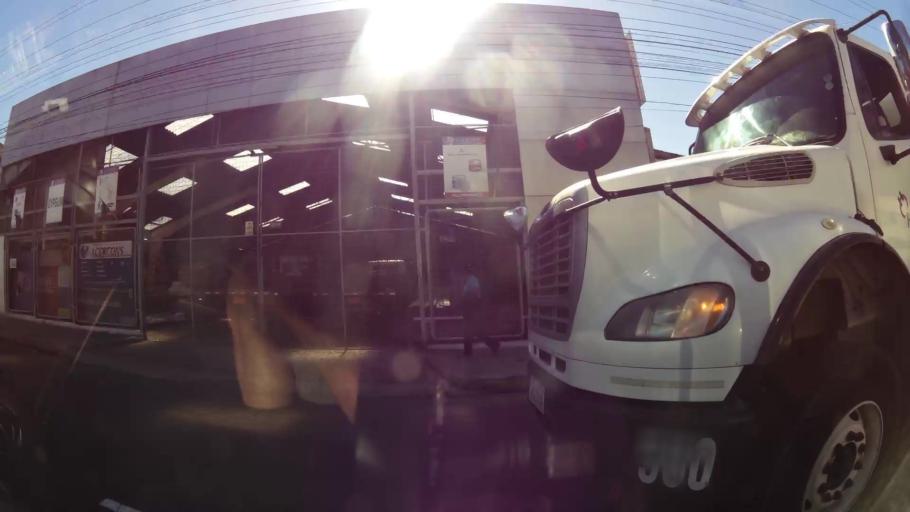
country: EC
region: Pichincha
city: Quito
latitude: -0.1619
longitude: -78.4759
